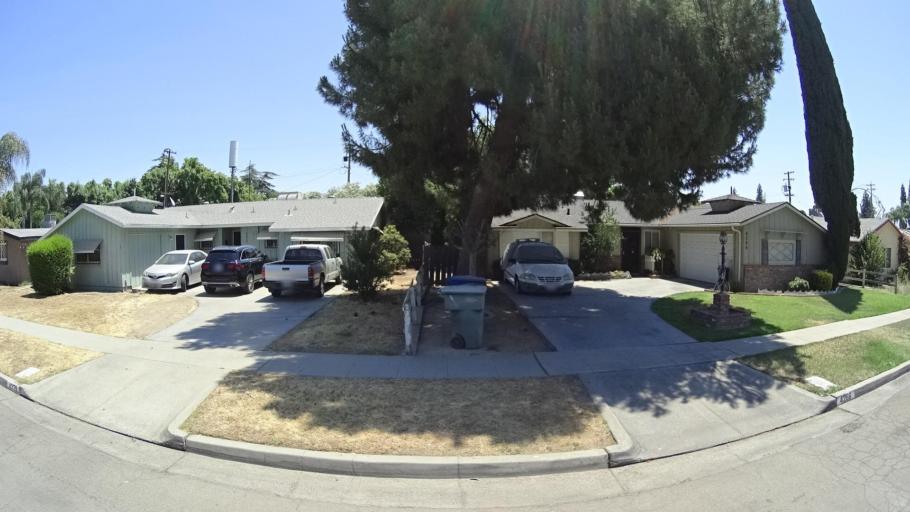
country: US
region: California
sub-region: Fresno County
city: Fresno
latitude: 36.7954
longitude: -119.7588
